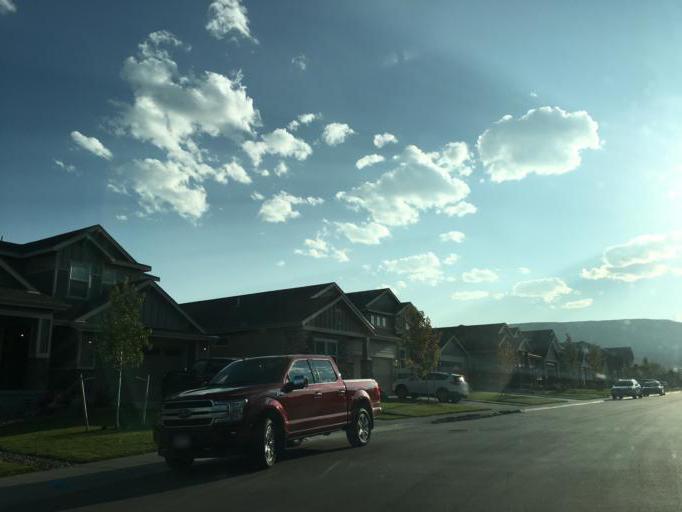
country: US
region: Colorado
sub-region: Jefferson County
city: Applewood
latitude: 39.7853
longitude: -105.1716
